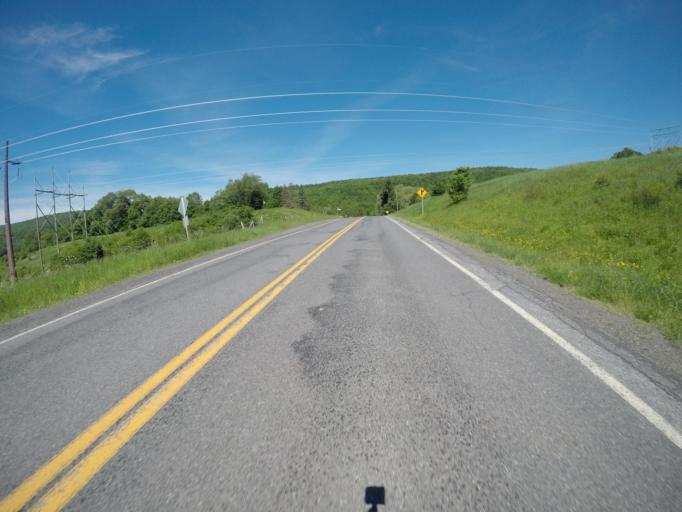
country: US
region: New York
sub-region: Delaware County
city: Delhi
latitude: 42.2154
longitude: -74.9021
